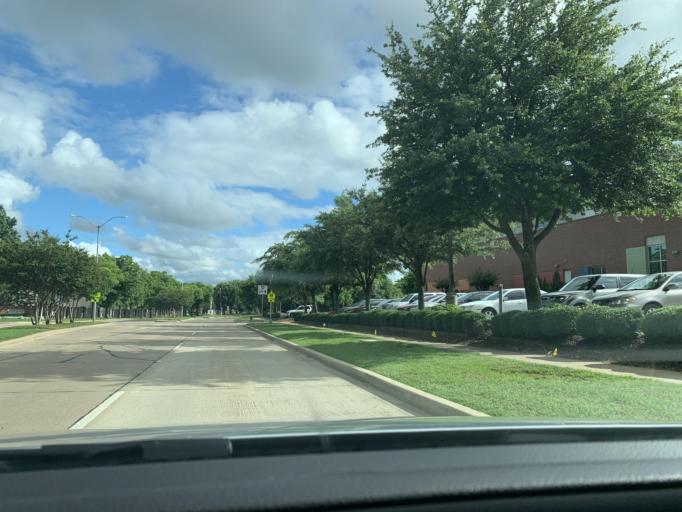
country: US
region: Texas
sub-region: Dallas County
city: Grand Prairie
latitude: 32.6616
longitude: -97.0027
